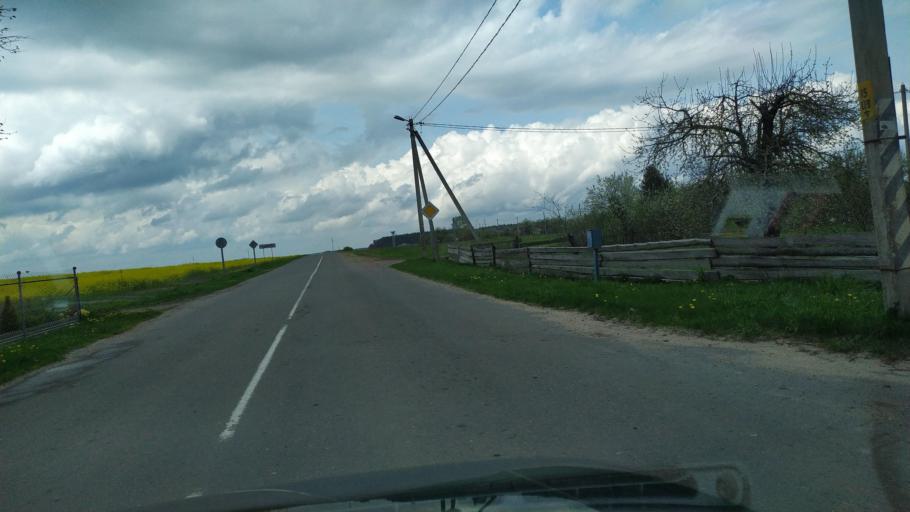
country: BY
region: Brest
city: Pruzhany
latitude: 52.6325
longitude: 24.3859
